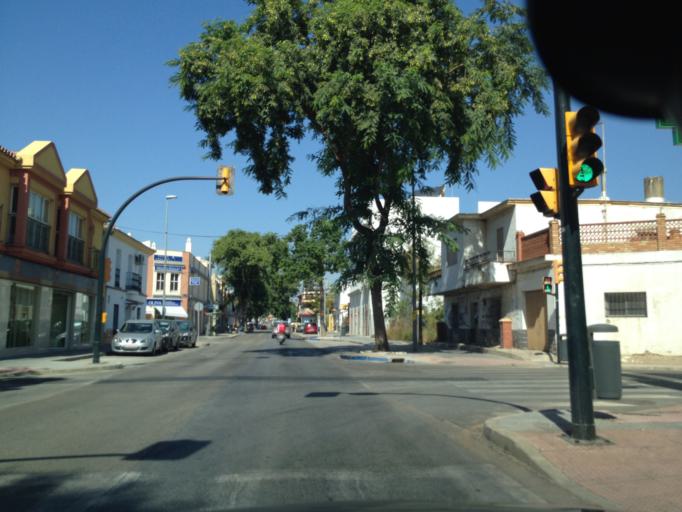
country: ES
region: Andalusia
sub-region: Provincia de Malaga
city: Alhaurin de la Torre
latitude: 36.7239
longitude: -4.5388
